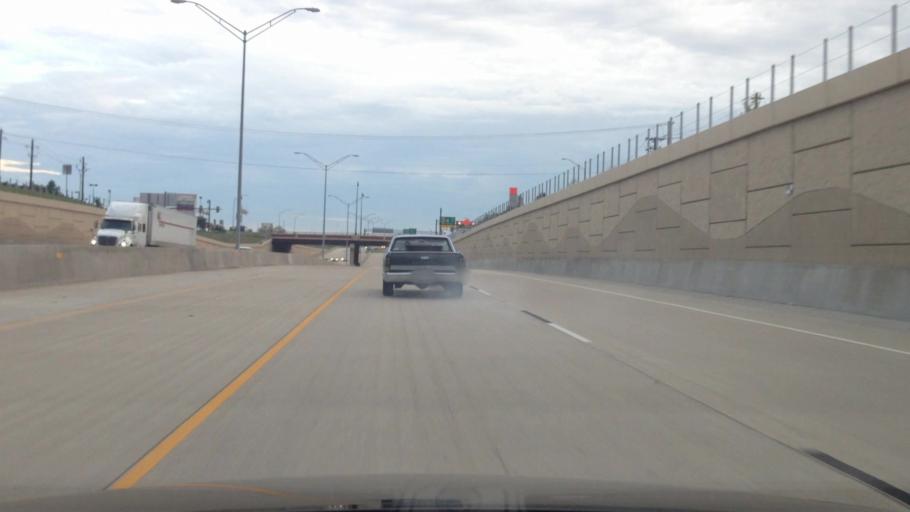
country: US
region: Texas
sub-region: Dallas County
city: Coppell
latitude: 32.9723
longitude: -97.0369
